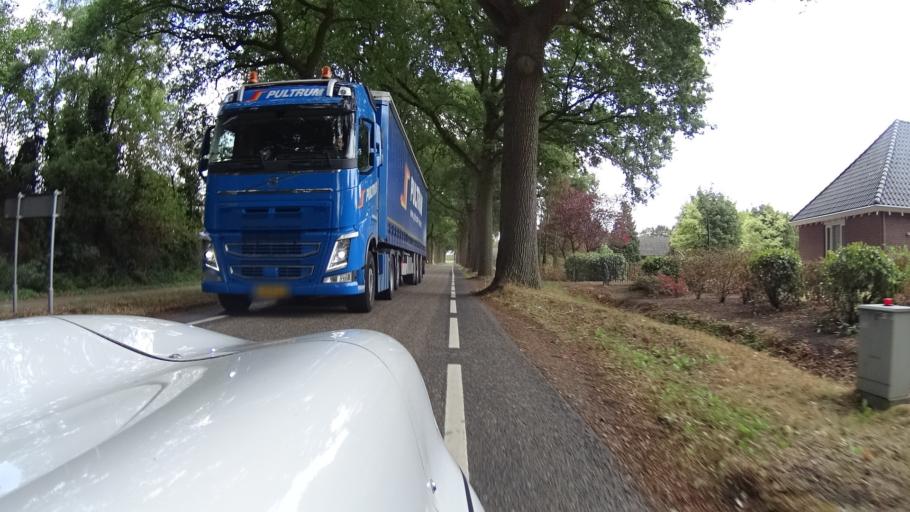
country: NL
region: North Brabant
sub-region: Gemeente Maasdonk
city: Geffen
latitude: 51.6951
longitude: 5.4479
